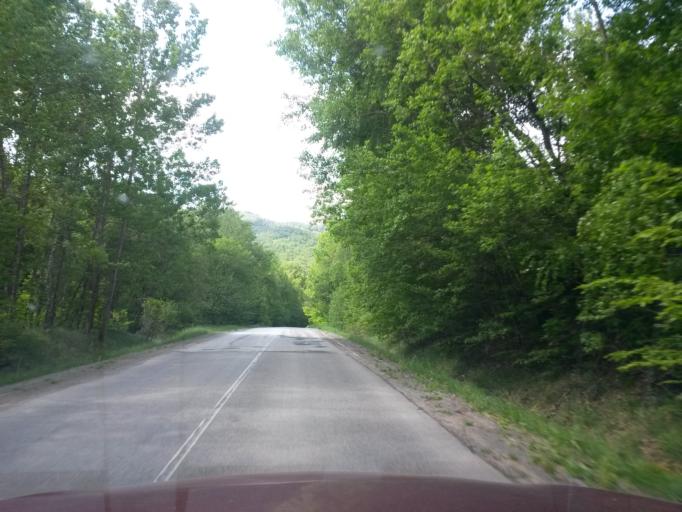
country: SK
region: Kosicky
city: Moldava nad Bodvou
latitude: 48.7281
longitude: 21.0859
